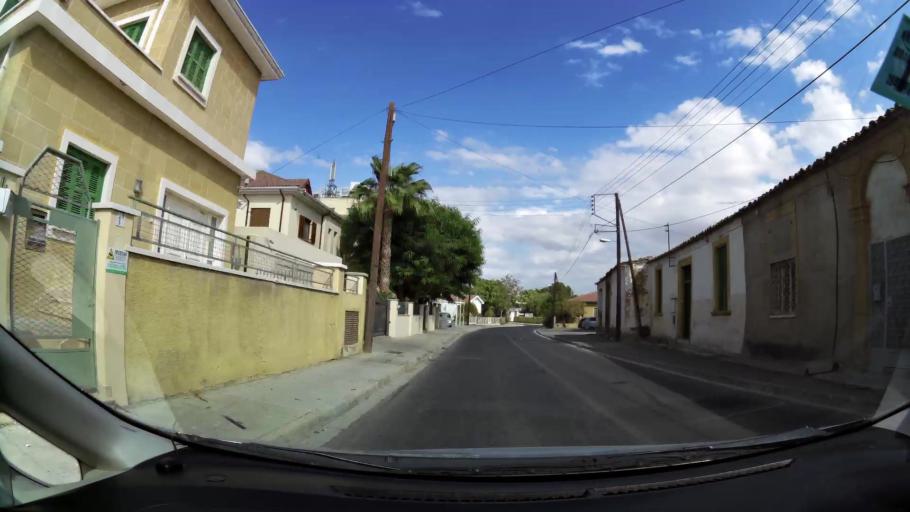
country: CY
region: Lefkosia
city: Nicosia
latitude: 35.1824
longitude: 33.3788
